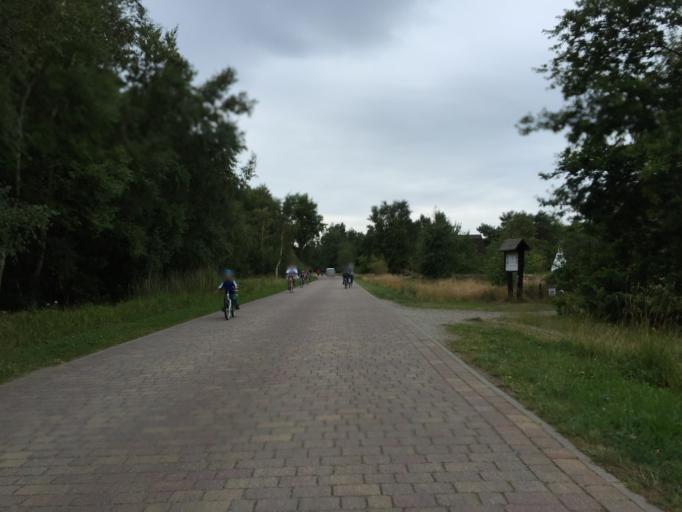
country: DE
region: Mecklenburg-Vorpommern
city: Hiddensee
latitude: 54.5487
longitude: 13.1063
